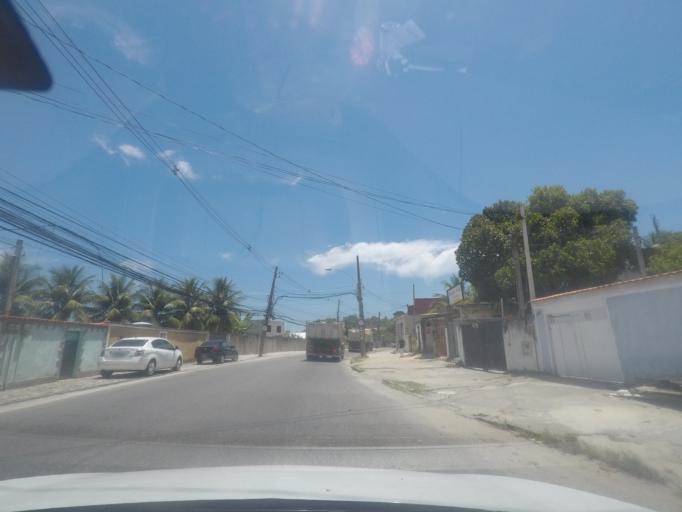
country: BR
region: Rio de Janeiro
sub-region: Itaguai
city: Itaguai
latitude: -22.9310
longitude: -43.6895
